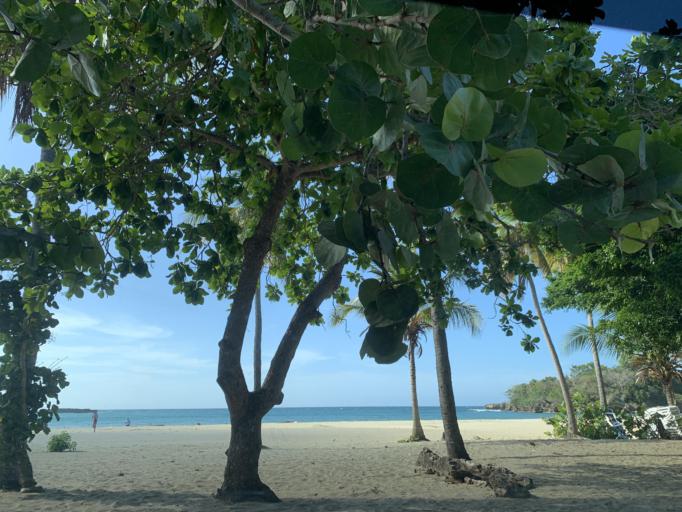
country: DO
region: Puerto Plata
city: Luperon
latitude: 19.9000
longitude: -70.8785
